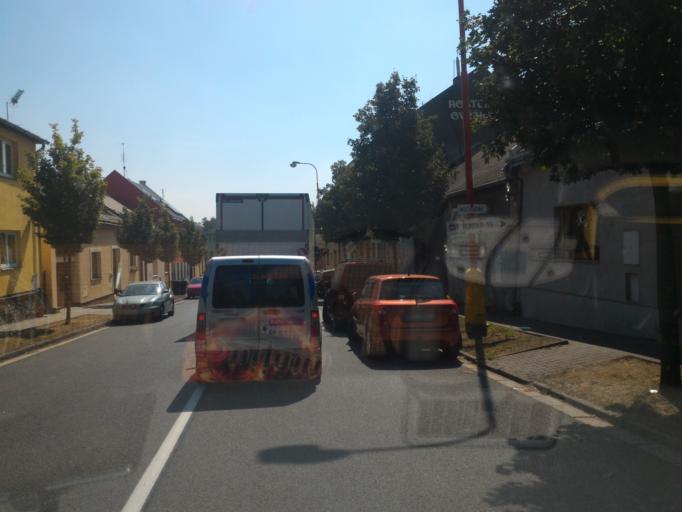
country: CZ
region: Pardubicky
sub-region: Okres Chrudim
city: Hlinsko
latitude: 49.7627
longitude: 15.8988
